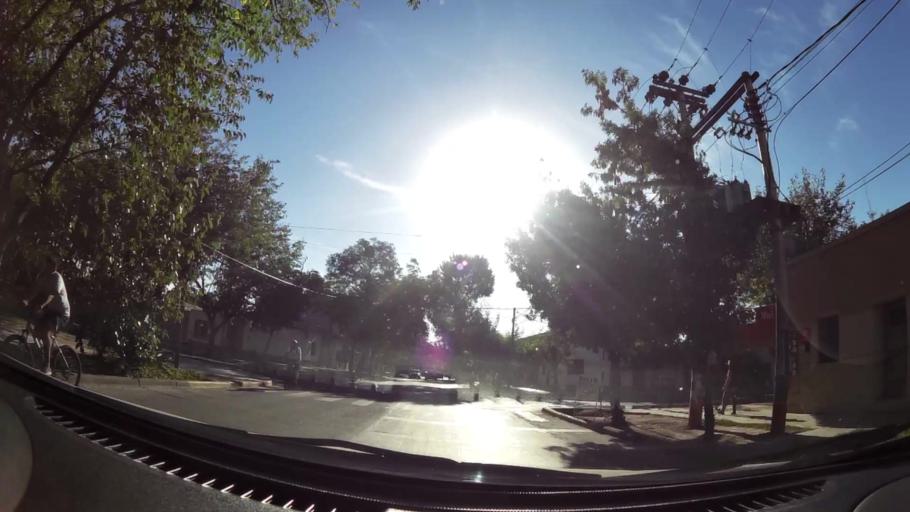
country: AR
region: Mendoza
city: Mendoza
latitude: -32.9003
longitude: -68.8213
